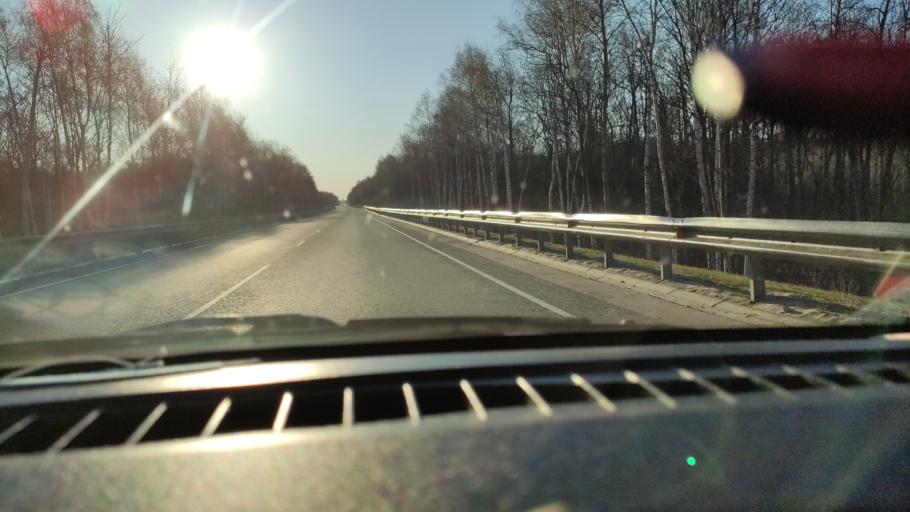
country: RU
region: Saratov
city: Vol'sk
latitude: 52.1113
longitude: 47.3345
